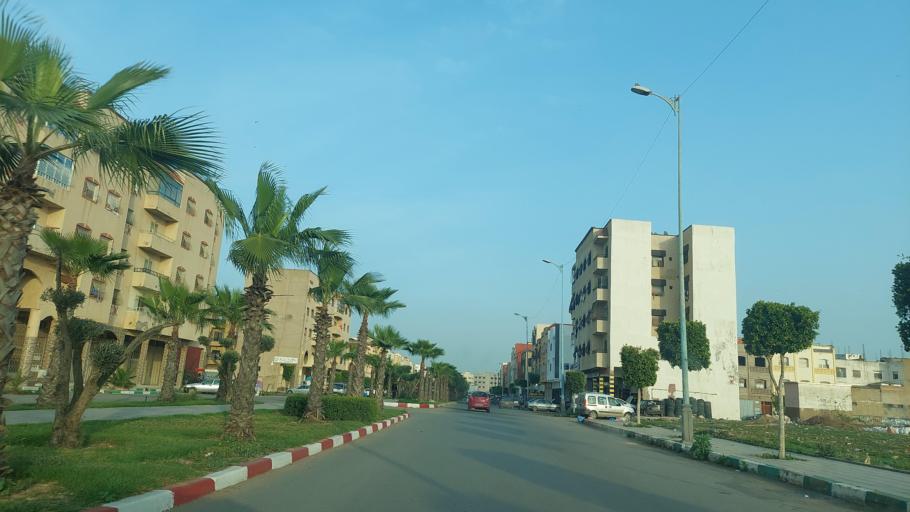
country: MA
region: Grand Casablanca
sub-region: Mediouna
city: Mediouna
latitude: 33.3830
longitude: -7.5380
